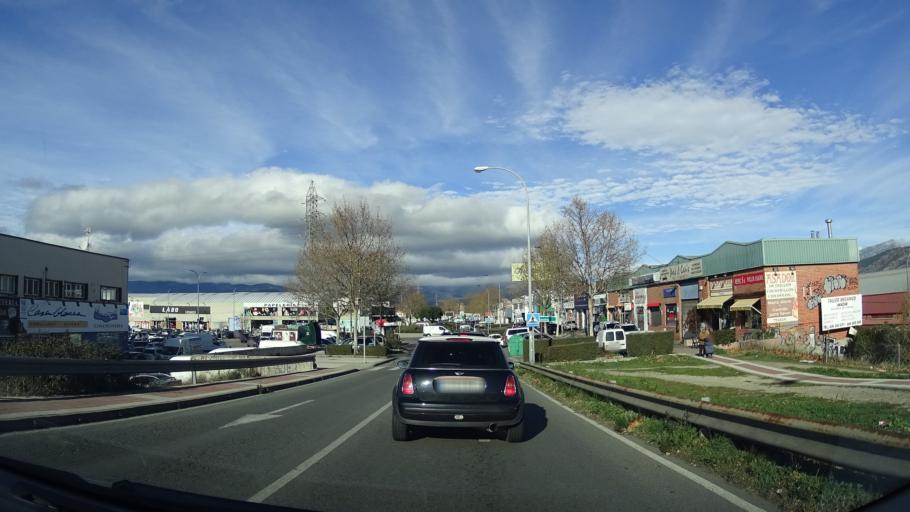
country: ES
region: Madrid
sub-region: Provincia de Madrid
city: Collado-Villalba
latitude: 40.6257
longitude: -4.0169
